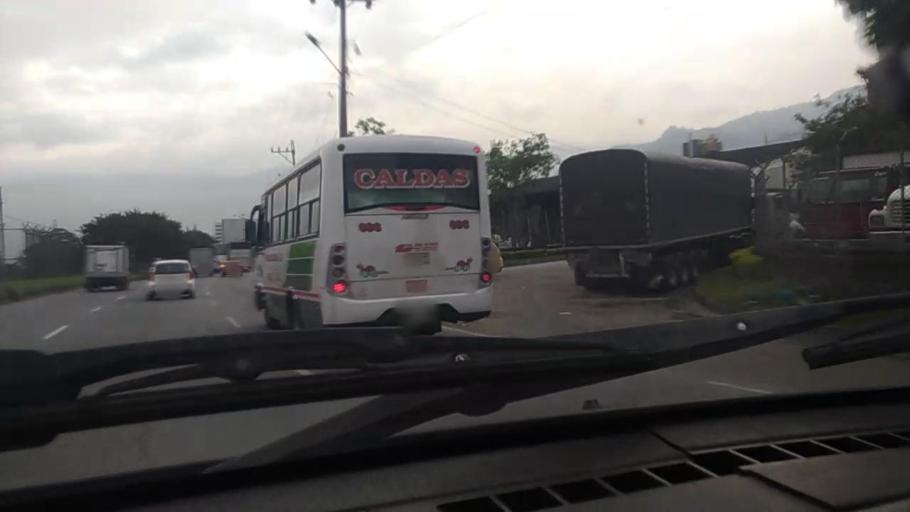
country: CO
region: Antioquia
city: Sabaneta
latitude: 6.1558
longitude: -75.6208
